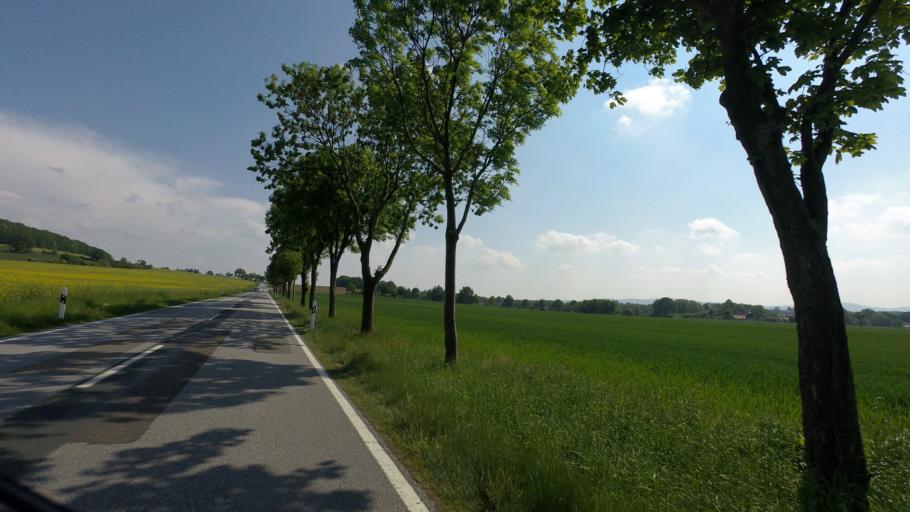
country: DE
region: Saxony
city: Weissenberg
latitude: 51.1835
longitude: 14.6438
